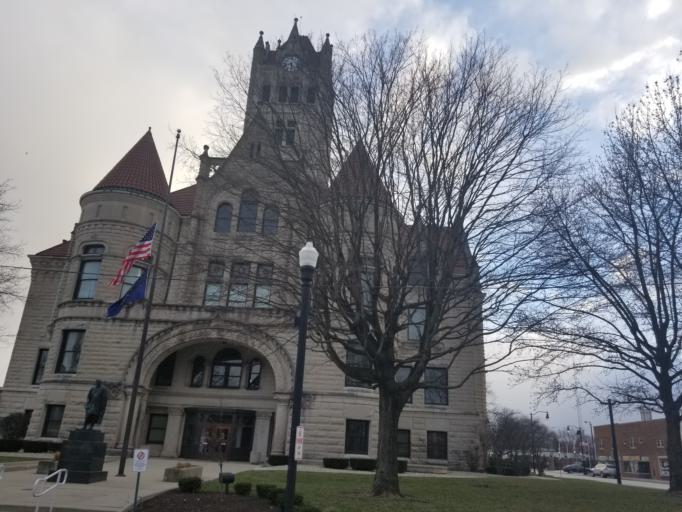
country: US
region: Indiana
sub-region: Hancock County
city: Greenfield
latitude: 39.7860
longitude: -85.7700
